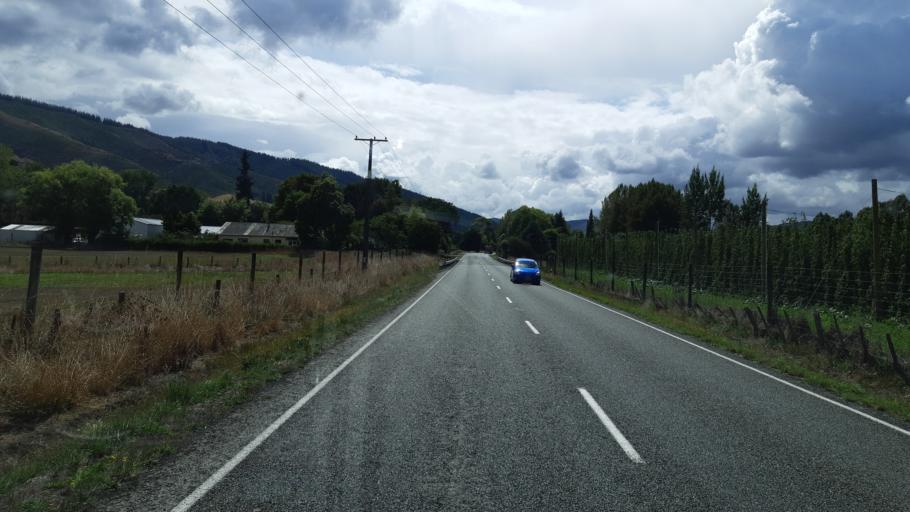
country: NZ
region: Tasman
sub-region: Tasman District
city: Wakefield
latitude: -41.4617
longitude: 172.8104
